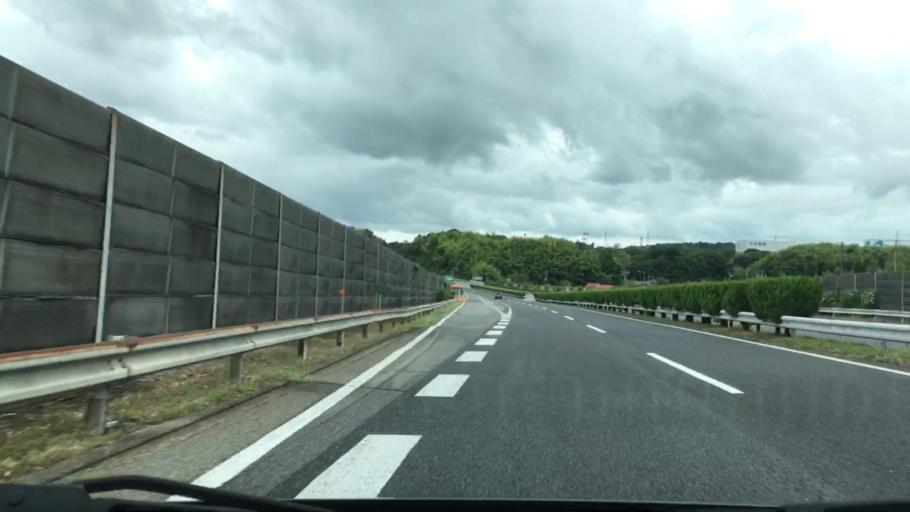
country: JP
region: Okayama
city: Tsuyama
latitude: 35.0433
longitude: 134.1191
